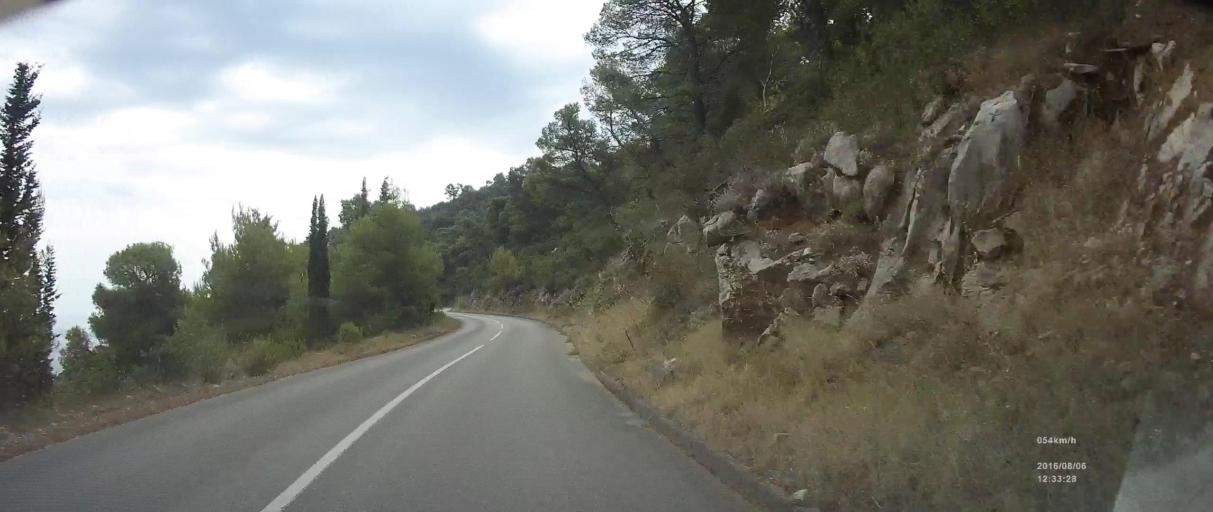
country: HR
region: Dubrovacko-Neretvanska
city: Ston
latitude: 42.7127
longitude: 17.7216
